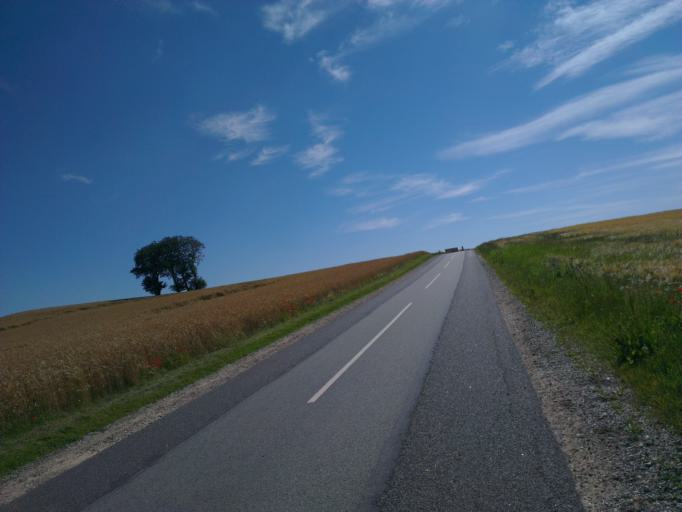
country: DK
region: Capital Region
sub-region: Frederikssund Kommune
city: Slangerup
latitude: 55.8566
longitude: 12.1415
